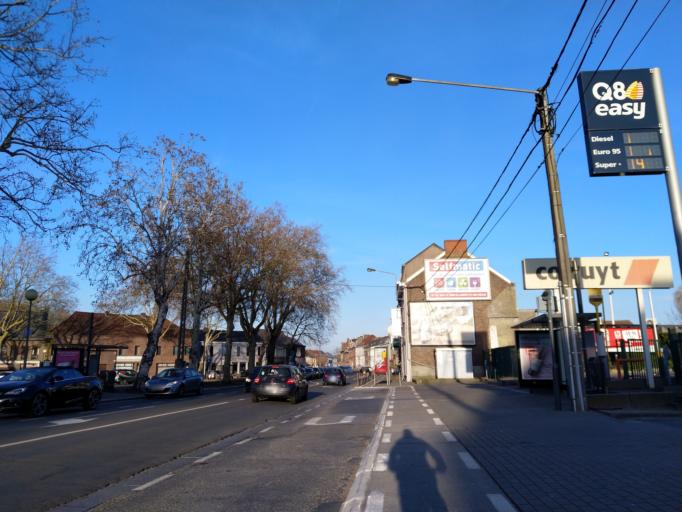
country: BE
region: Wallonia
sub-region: Province du Hainaut
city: Chasse Royale
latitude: 50.4365
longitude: 3.9251
